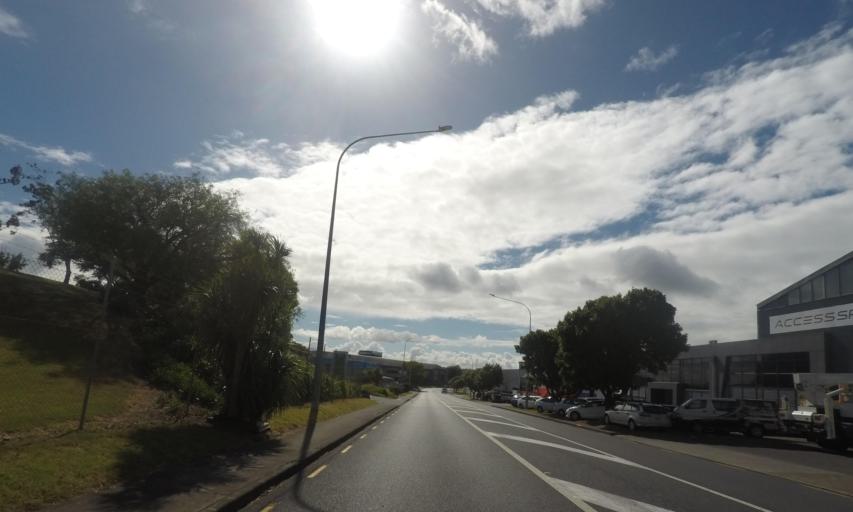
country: NZ
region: Auckland
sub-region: Auckland
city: Tamaki
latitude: -36.9208
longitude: 174.8492
